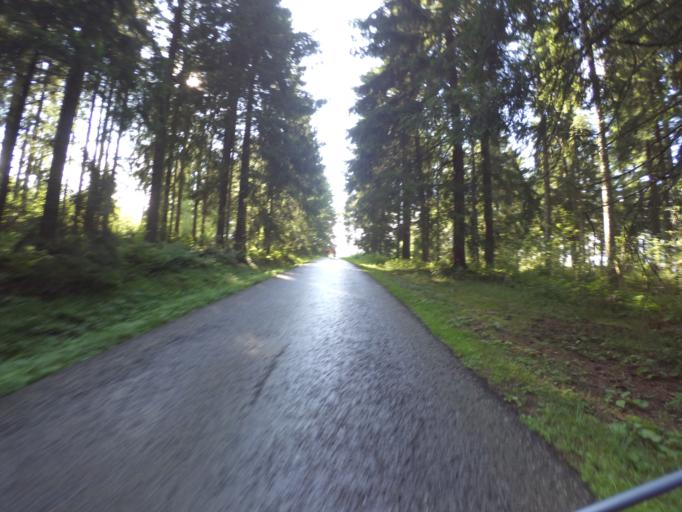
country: DE
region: Baden-Wuerttemberg
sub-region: Freiburg Region
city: Titisee-Neustadt
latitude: 47.9010
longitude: 8.1861
